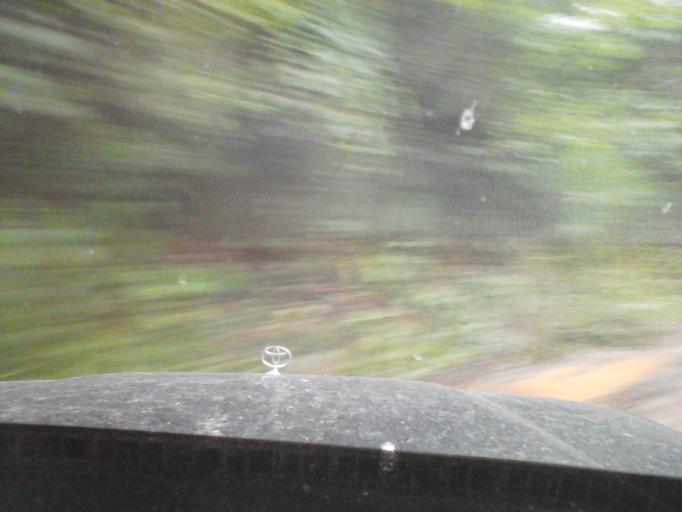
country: CO
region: Cesar
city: Agustin Codazzi
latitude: 9.9402
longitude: -73.1343
